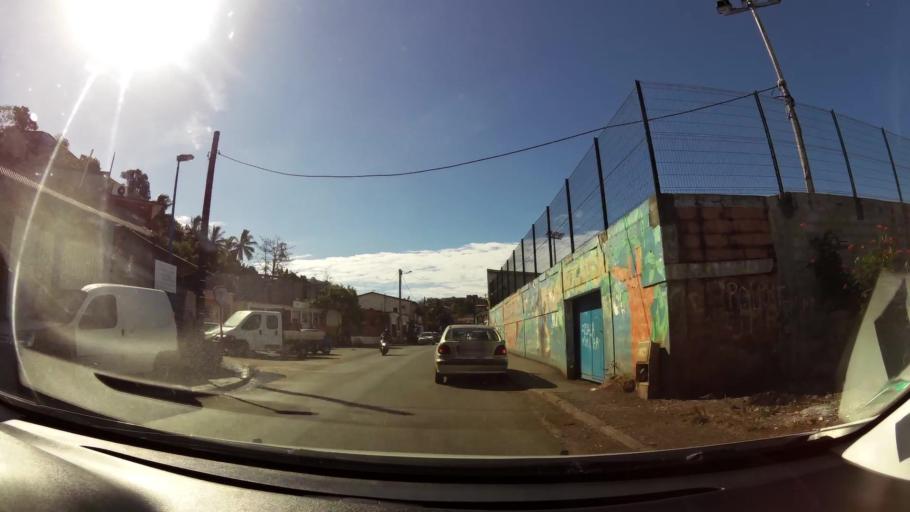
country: YT
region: Mamoudzou
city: Mamoudzou
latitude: -12.7910
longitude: 45.2204
